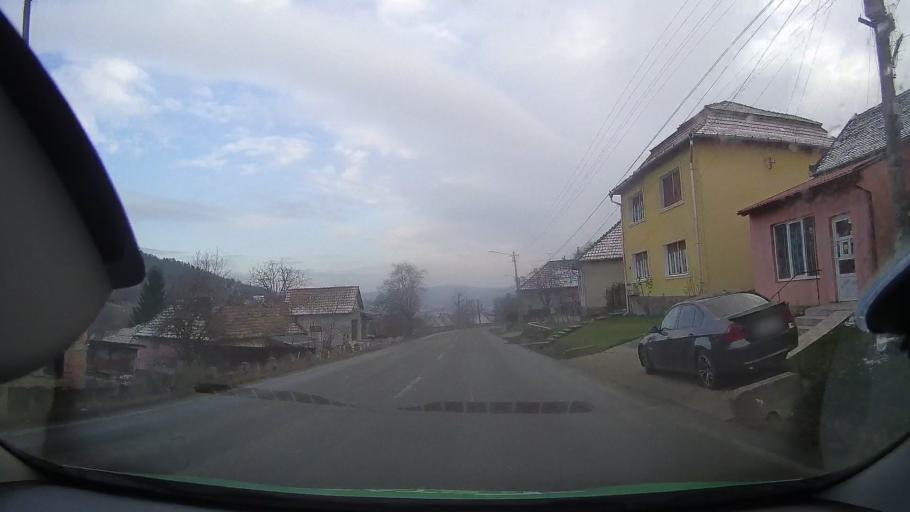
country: RO
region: Mures
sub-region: Municipiul Tarnaveni
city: Tarnaveni
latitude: 46.3382
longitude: 24.2845
